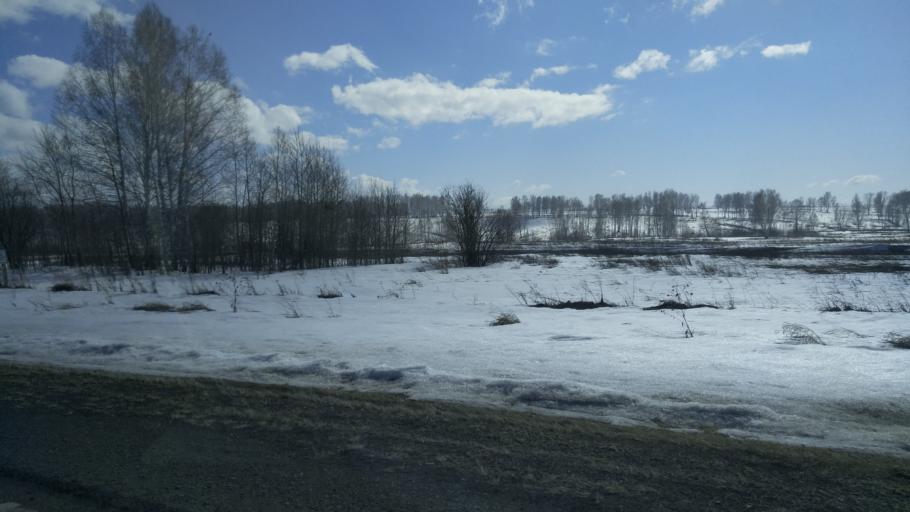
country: RU
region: Kemerovo
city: Yurga
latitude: 55.6847
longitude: 85.0552
